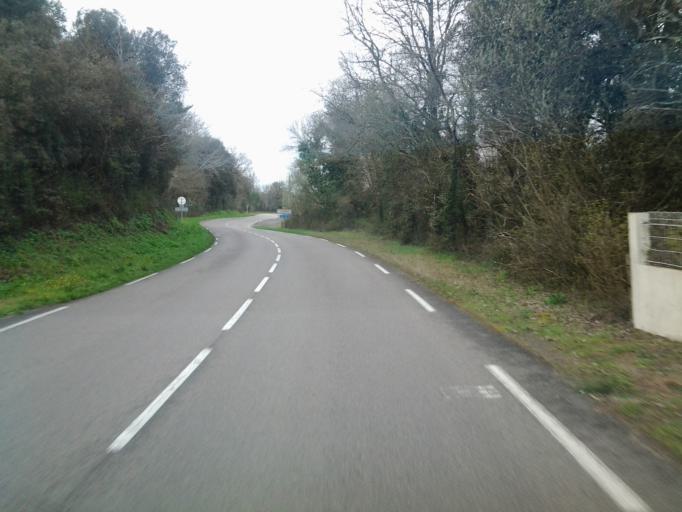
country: FR
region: Pays de la Loire
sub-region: Departement de la Vendee
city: Longeville-sur-Mer
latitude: 46.3994
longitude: -1.4843
